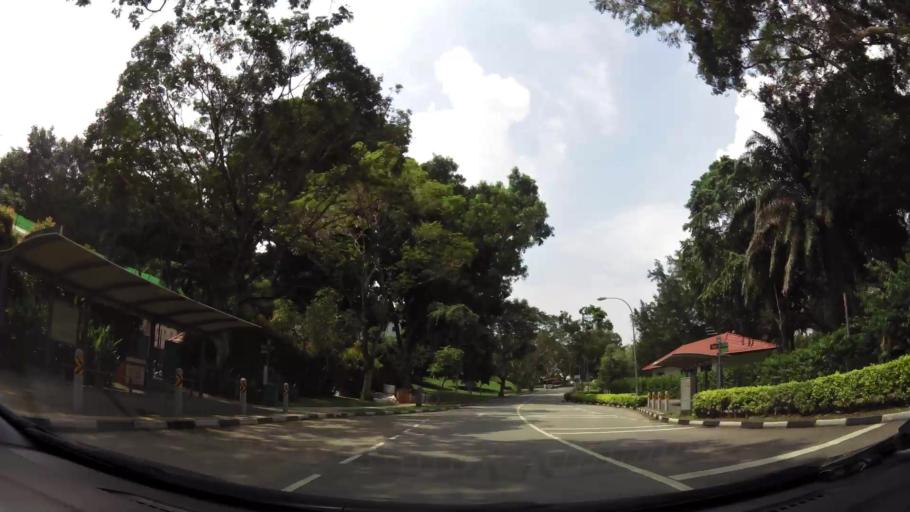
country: MY
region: Johor
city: Kampung Pasir Gudang Baru
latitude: 1.3913
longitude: 103.9819
